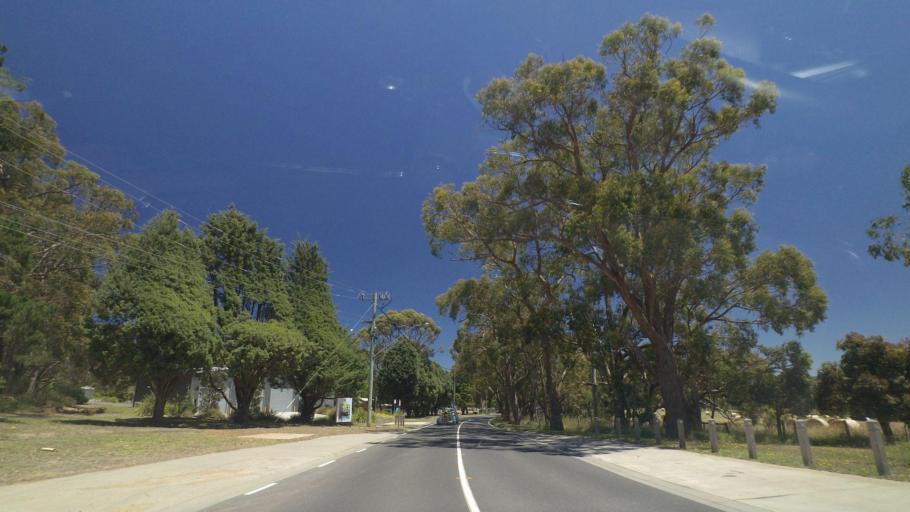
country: AU
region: Victoria
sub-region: Mornington Peninsula
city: McCrae
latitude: -38.3991
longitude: 144.9714
